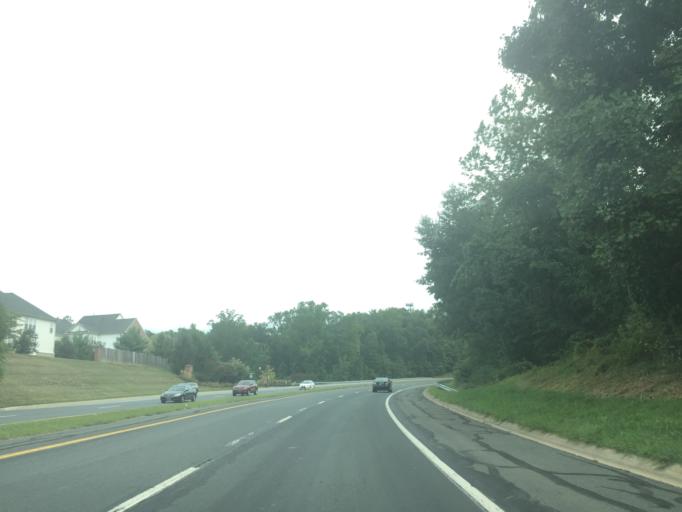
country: US
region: Maryland
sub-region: Montgomery County
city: Gaithersburg
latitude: 39.1571
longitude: -77.1852
